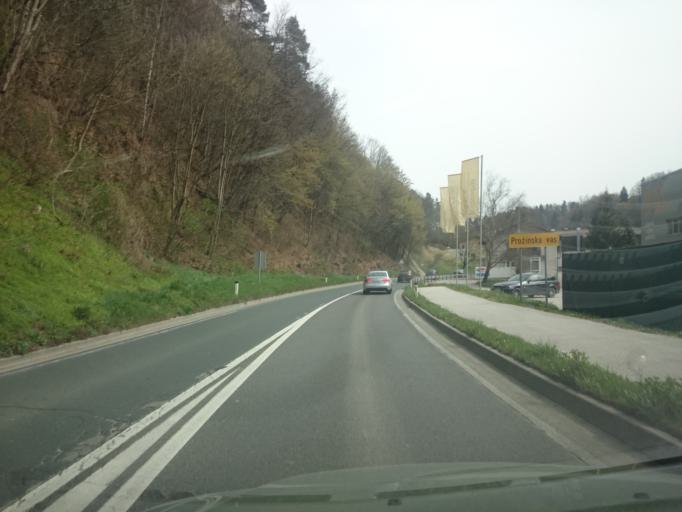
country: SI
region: Store
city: Store
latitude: 46.2217
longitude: 15.3310
